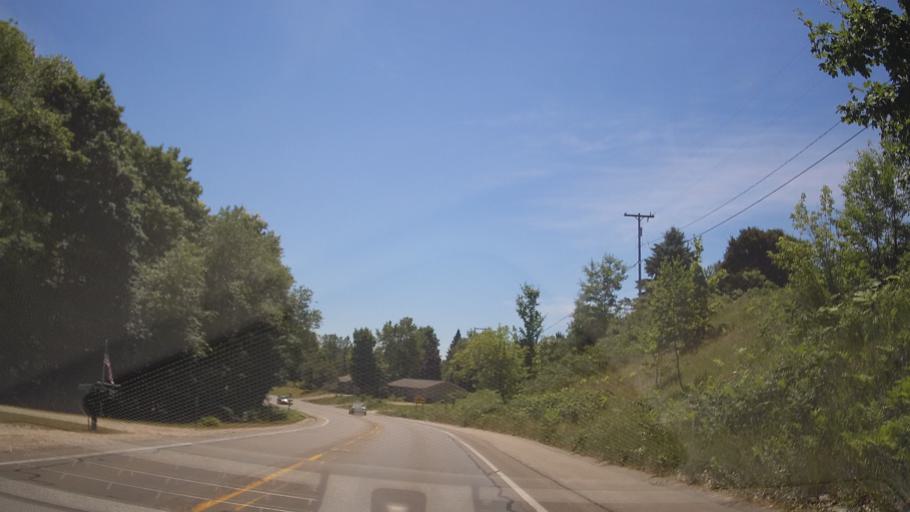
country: US
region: Michigan
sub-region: Grand Traverse County
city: Traverse City
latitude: 44.7110
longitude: -85.6912
